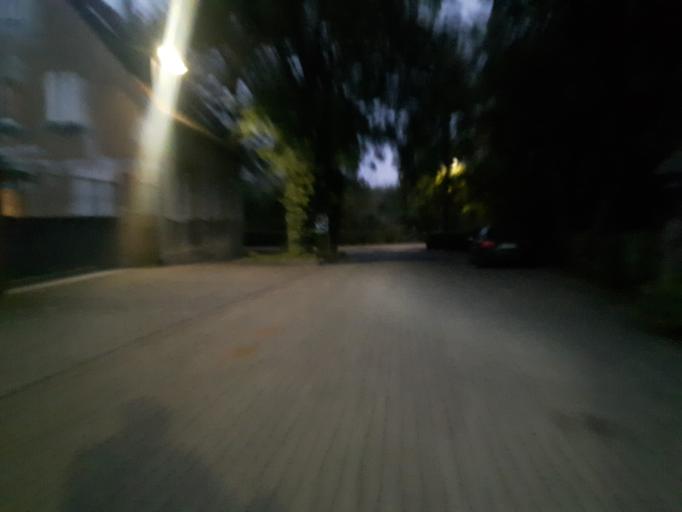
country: DE
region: Rheinland-Pfalz
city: Flomborn
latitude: 49.6934
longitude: 8.1505
